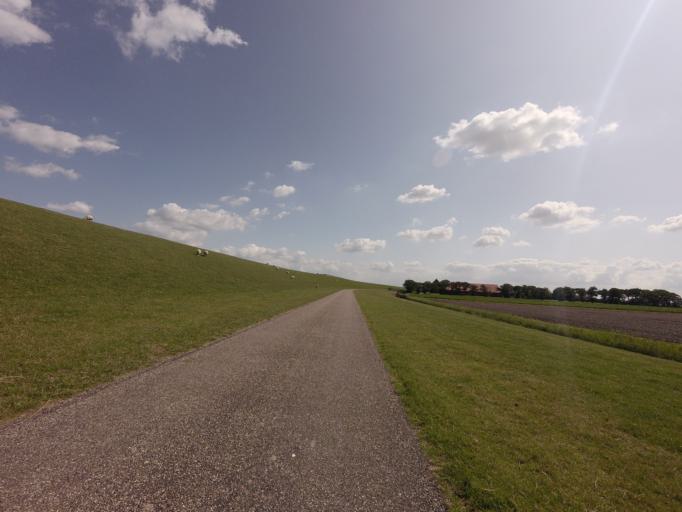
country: NL
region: Friesland
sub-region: Gemeente Ferwerderadiel
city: Hallum
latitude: 53.3237
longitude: 5.7368
